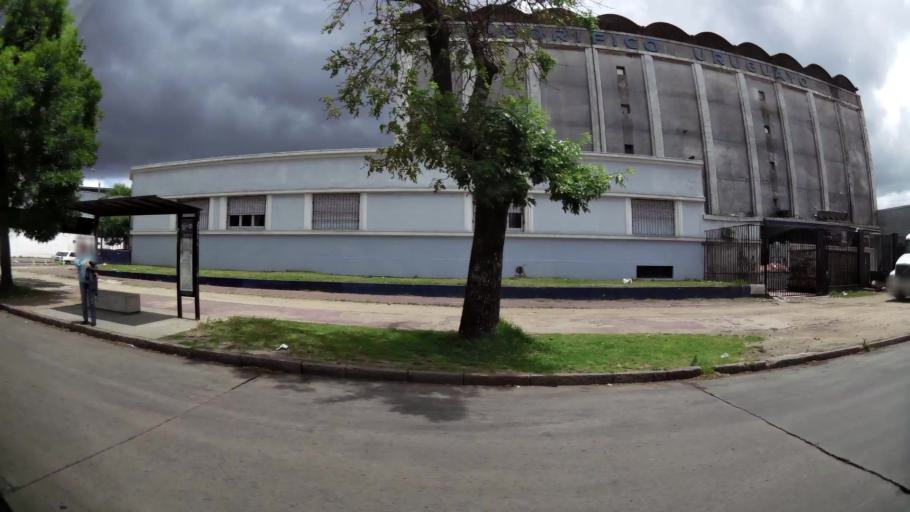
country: UY
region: Montevideo
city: Montevideo
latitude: -34.8710
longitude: -56.1523
